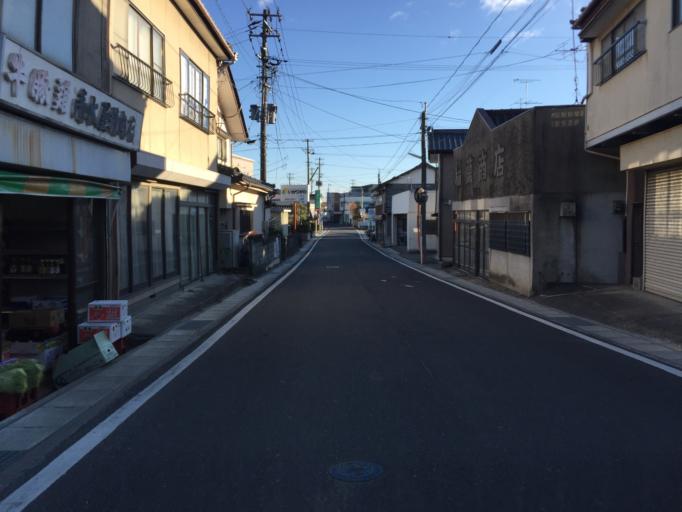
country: JP
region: Fukushima
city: Iwaki
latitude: 37.1283
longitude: 140.8612
